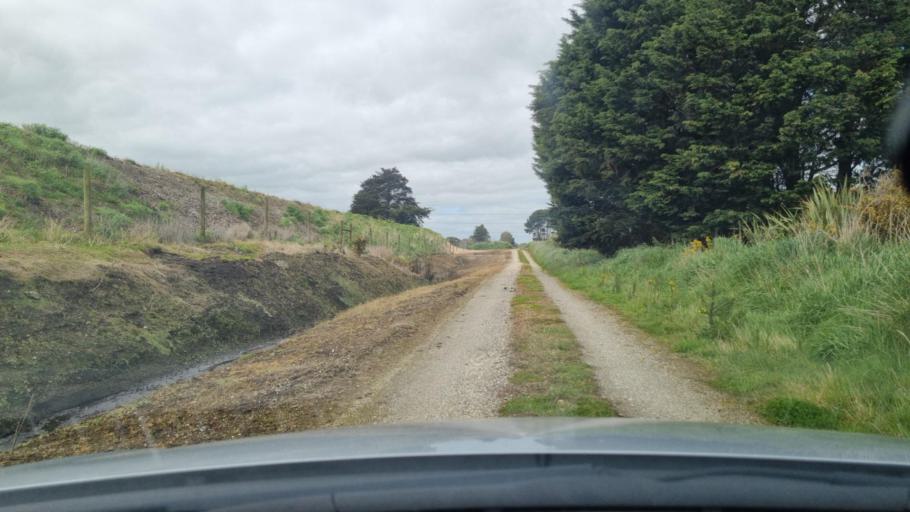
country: NZ
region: Southland
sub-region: Invercargill City
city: Invercargill
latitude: -46.3922
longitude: 168.4581
